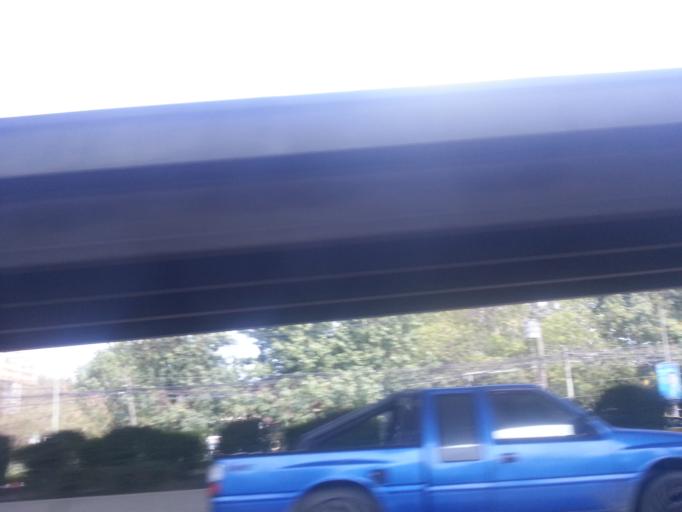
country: TH
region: Bangkok
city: Don Mueang
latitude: 13.8982
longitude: 100.5918
